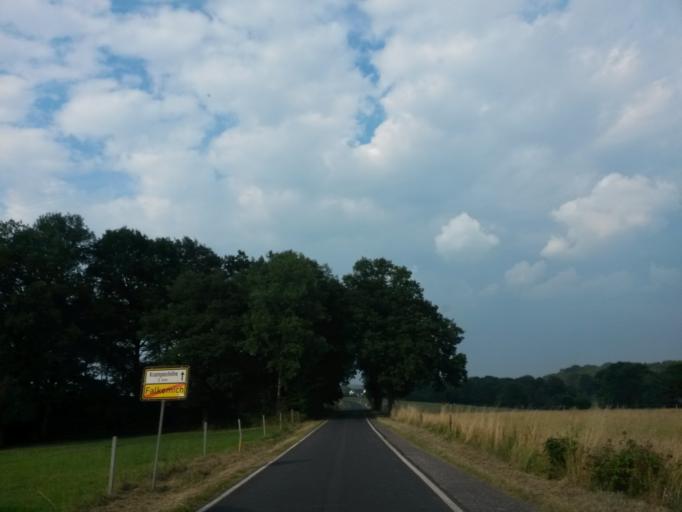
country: DE
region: North Rhine-Westphalia
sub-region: Regierungsbezirk Koln
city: Overath
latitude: 50.9198
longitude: 7.3383
